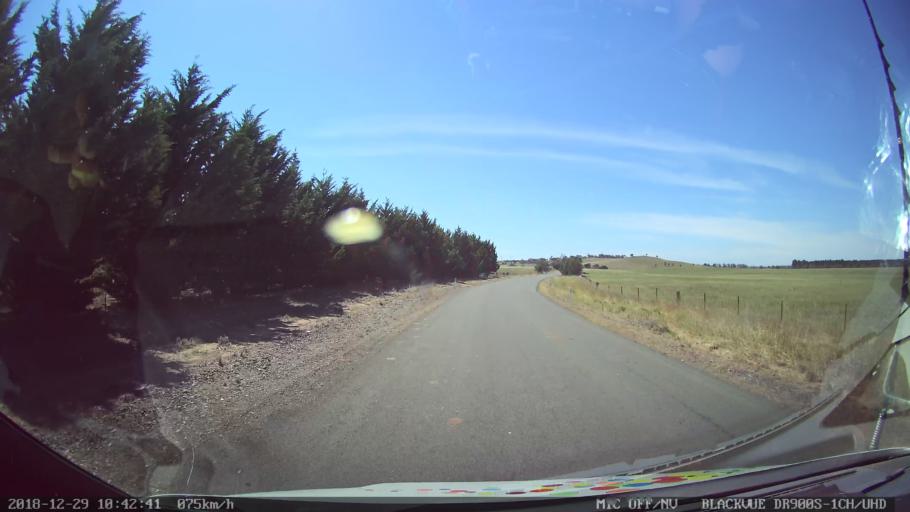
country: AU
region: New South Wales
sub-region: Palerang
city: Bungendore
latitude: -35.0347
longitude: 149.5330
